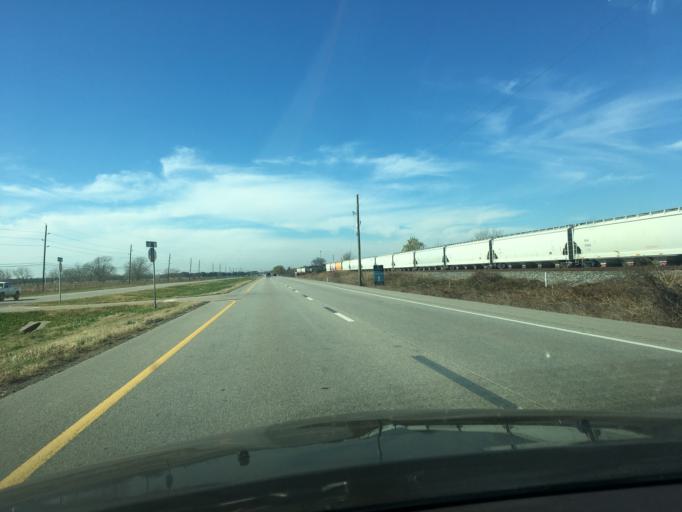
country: US
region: Texas
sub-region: Fort Bend County
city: New Territory
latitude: 29.5999
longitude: -95.7033
